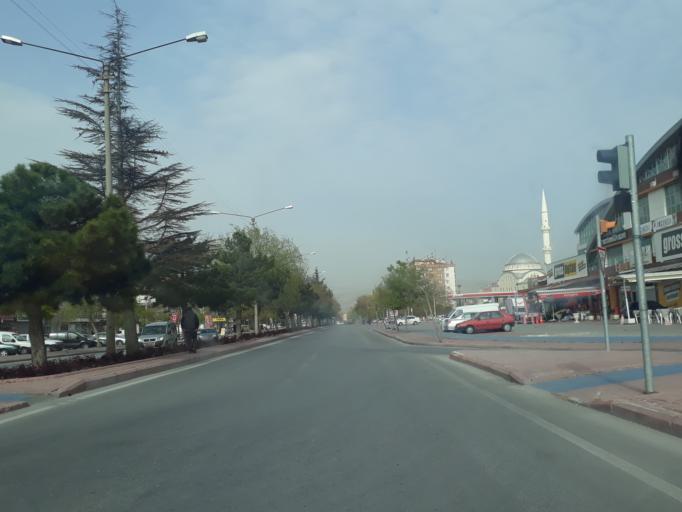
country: TR
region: Konya
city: Selcuklu
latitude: 37.9372
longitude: 32.5034
